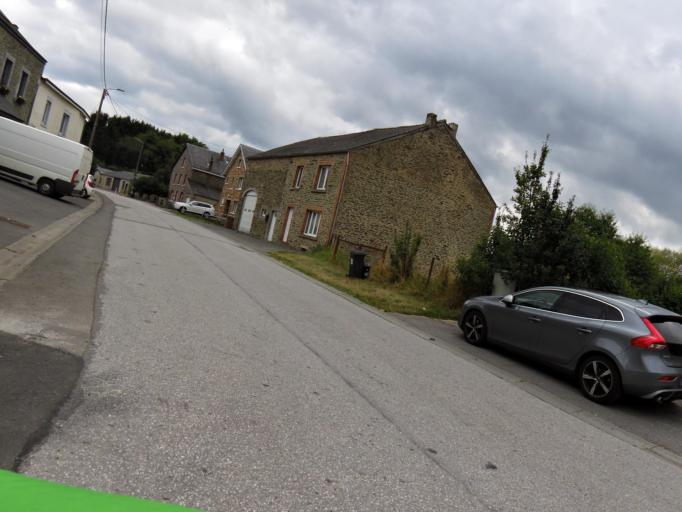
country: BE
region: Wallonia
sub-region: Province de Namur
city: Bievre
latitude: 49.9396
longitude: 5.0169
